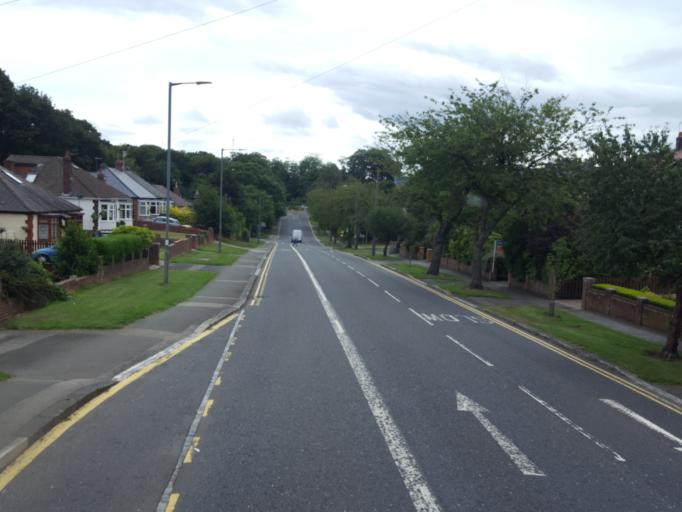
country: GB
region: England
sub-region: County Durham
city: Durham
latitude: 54.7923
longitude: -1.5904
